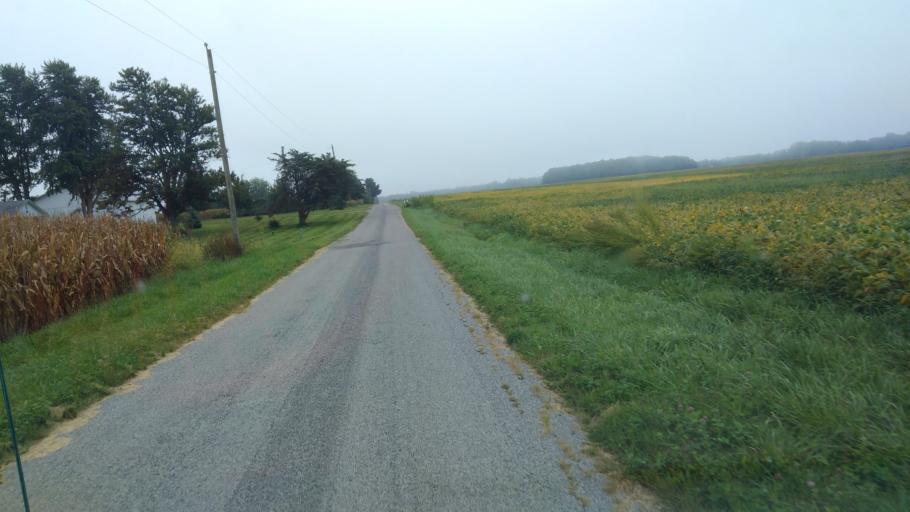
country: US
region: Ohio
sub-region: Union County
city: Richwood
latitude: 40.4956
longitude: -83.4141
